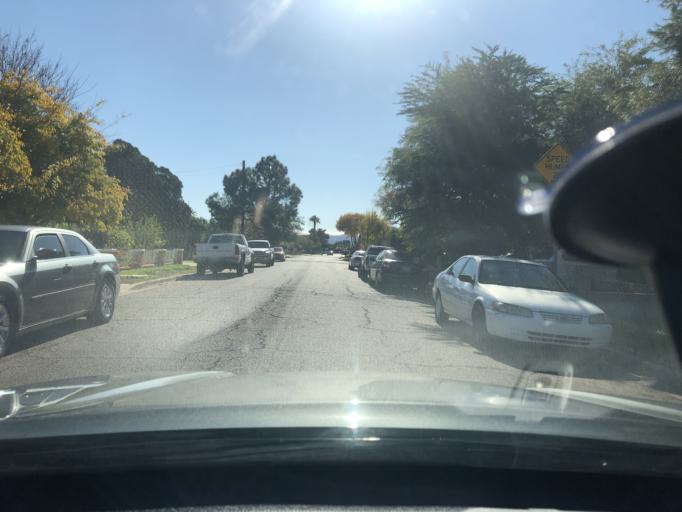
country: US
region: Arizona
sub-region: Maricopa County
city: Phoenix
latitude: 33.4715
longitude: -112.0278
